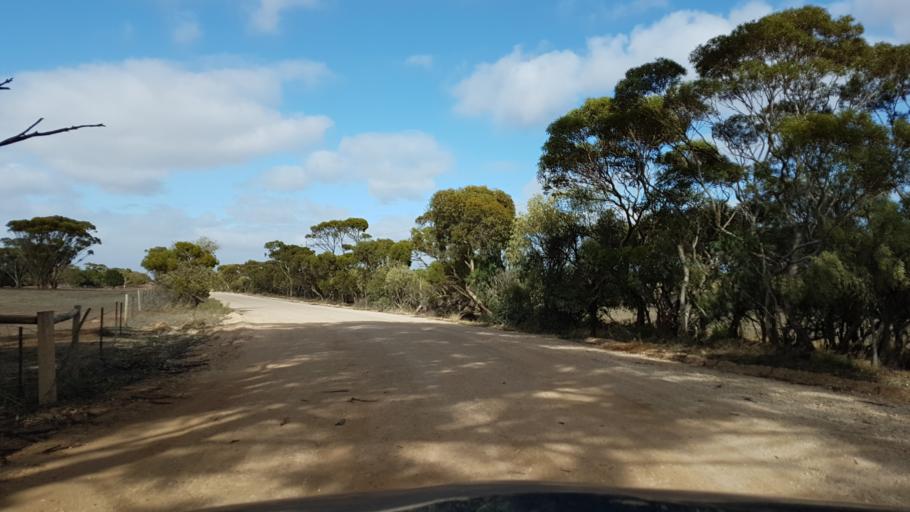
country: AU
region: South Australia
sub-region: Murray Bridge
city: Murray Bridge
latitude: -35.1131
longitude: 139.1969
